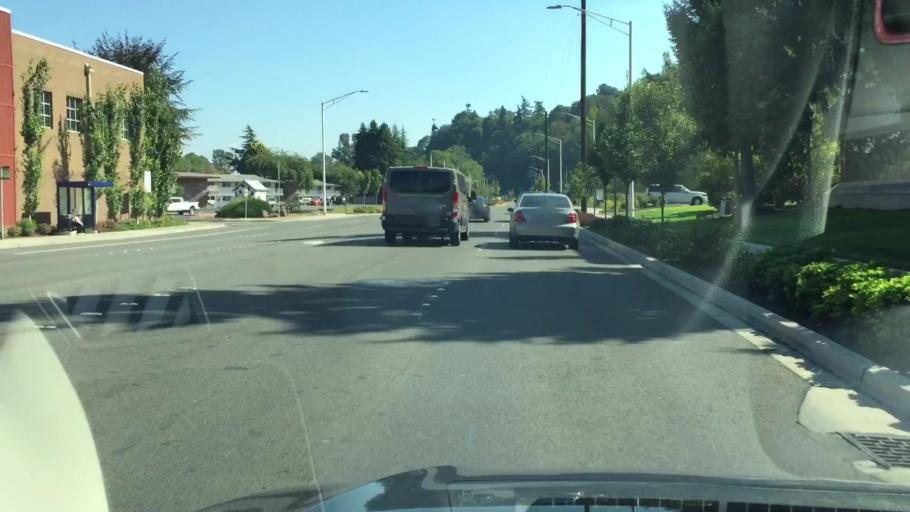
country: US
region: Washington
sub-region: King County
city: Tukwila
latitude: 47.4719
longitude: -122.2548
